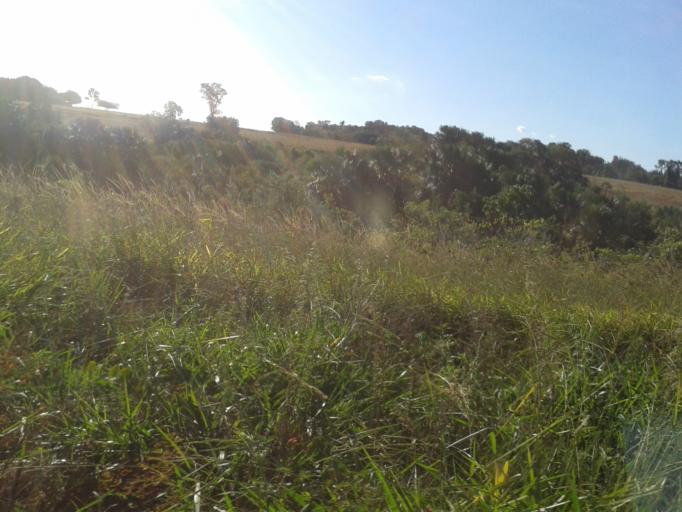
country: BR
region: Minas Gerais
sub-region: Centralina
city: Centralina
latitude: -18.7510
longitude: -49.1028
